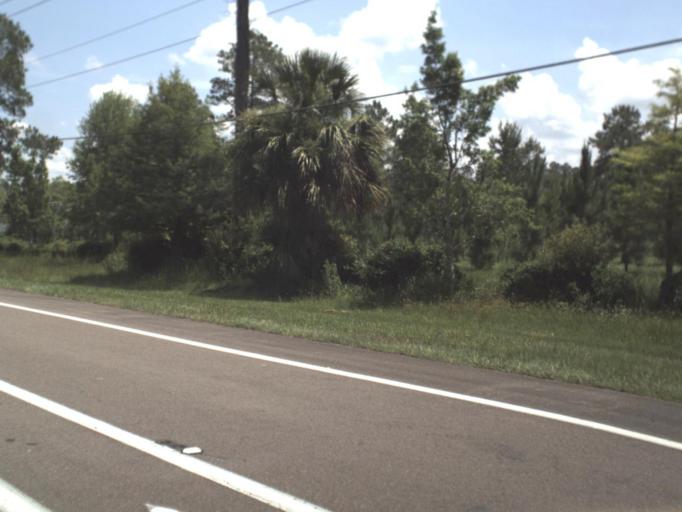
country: US
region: Florida
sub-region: Alachua County
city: Gainesville
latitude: 29.7152
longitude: -82.3535
